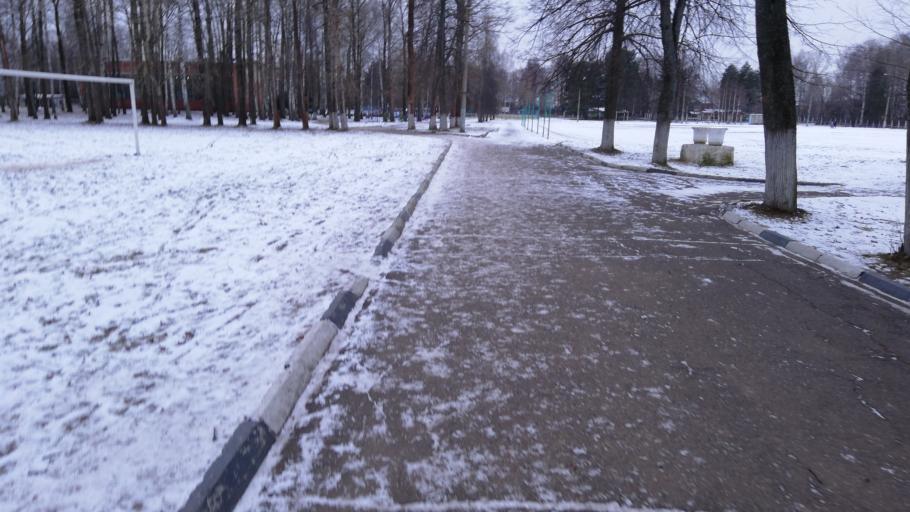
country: RU
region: Jaroslavl
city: Yaroslavl
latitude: 57.7242
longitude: 39.8164
